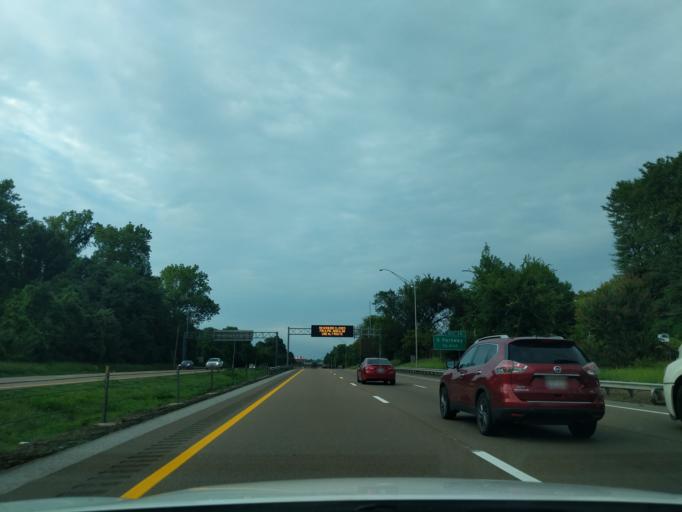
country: US
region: Tennessee
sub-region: Shelby County
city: New South Memphis
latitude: 35.0974
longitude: -90.0763
